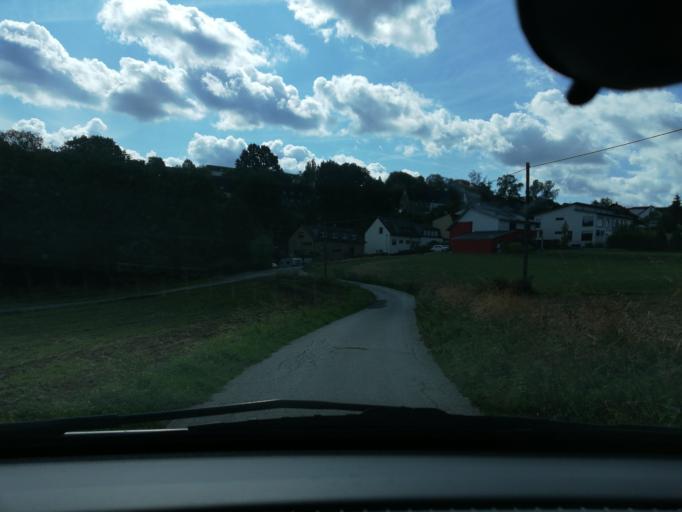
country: DE
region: North Rhine-Westphalia
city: Wetter (Ruhr)
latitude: 51.3785
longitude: 7.3660
